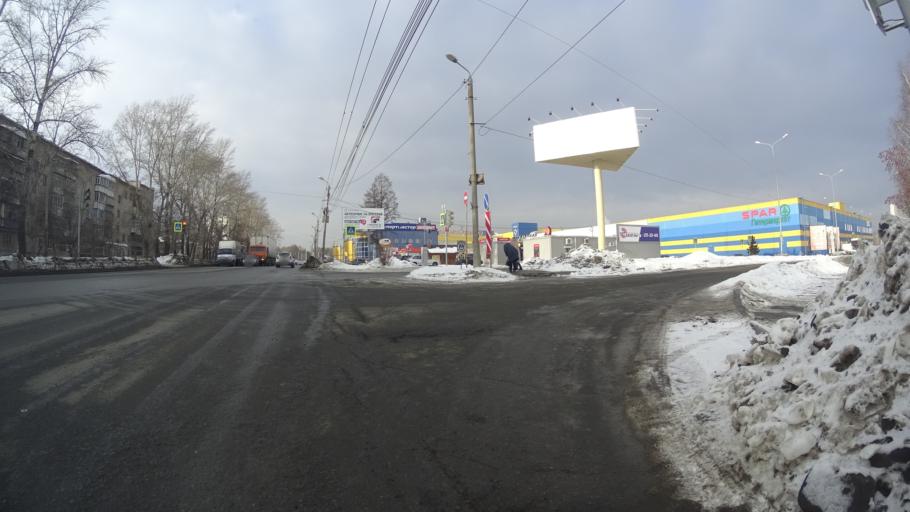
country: RU
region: Chelyabinsk
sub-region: Gorod Chelyabinsk
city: Chelyabinsk
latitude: 55.1251
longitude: 61.3706
